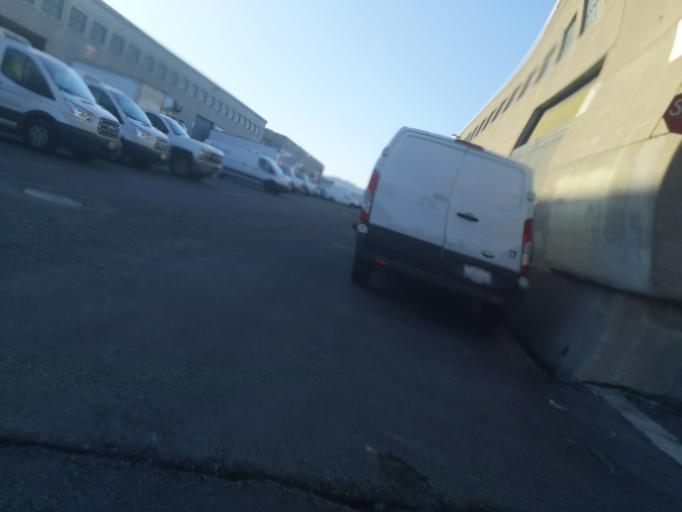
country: US
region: California
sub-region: San Francisco County
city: San Francisco
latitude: 37.8101
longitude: -122.4177
